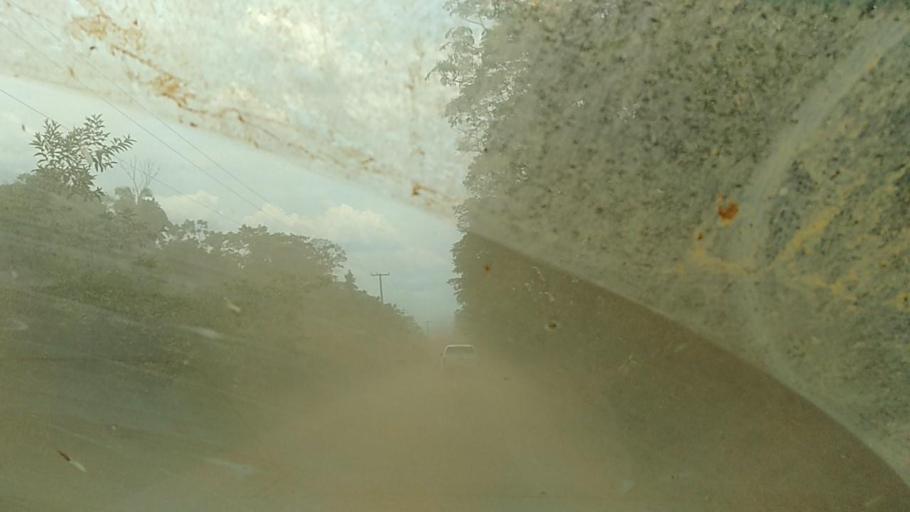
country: BR
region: Rondonia
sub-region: Porto Velho
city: Porto Velho
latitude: -8.9567
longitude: -64.3206
